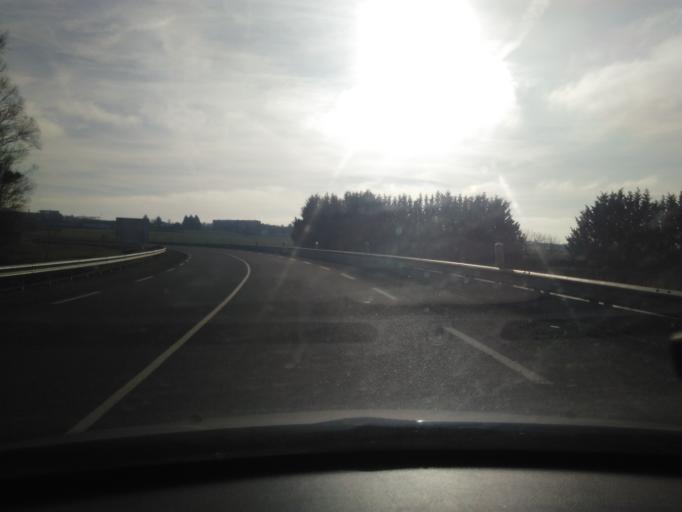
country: FR
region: Bourgogne
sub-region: Departement de la Nievre
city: Magny-Cours
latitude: 46.8714
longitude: 3.1551
